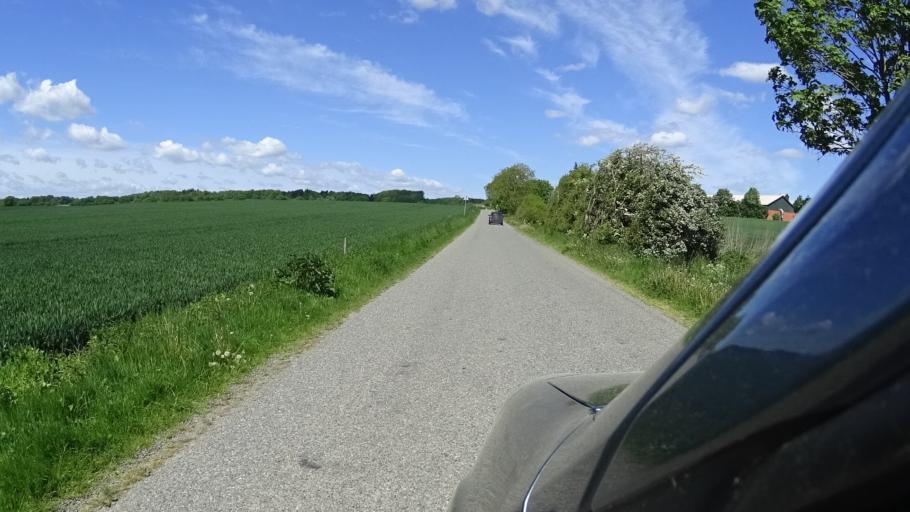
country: DK
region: South Denmark
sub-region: Vejle Kommune
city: Borkop
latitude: 55.6113
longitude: 9.6487
